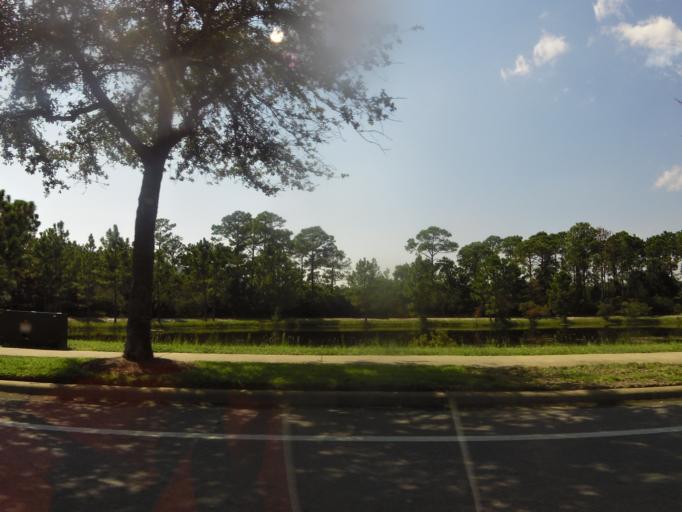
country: US
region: Florida
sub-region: Bay County
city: Laguna Beach
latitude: 30.2211
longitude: -85.8733
